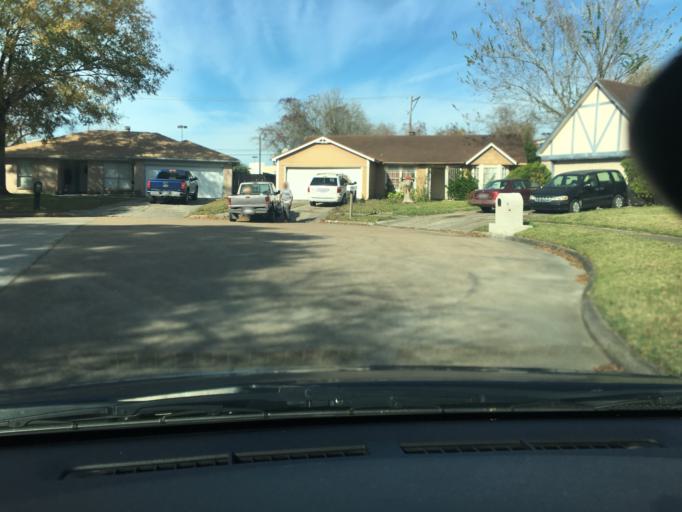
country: US
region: Texas
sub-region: Harris County
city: Cloverleaf
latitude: 29.8087
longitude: -95.1606
